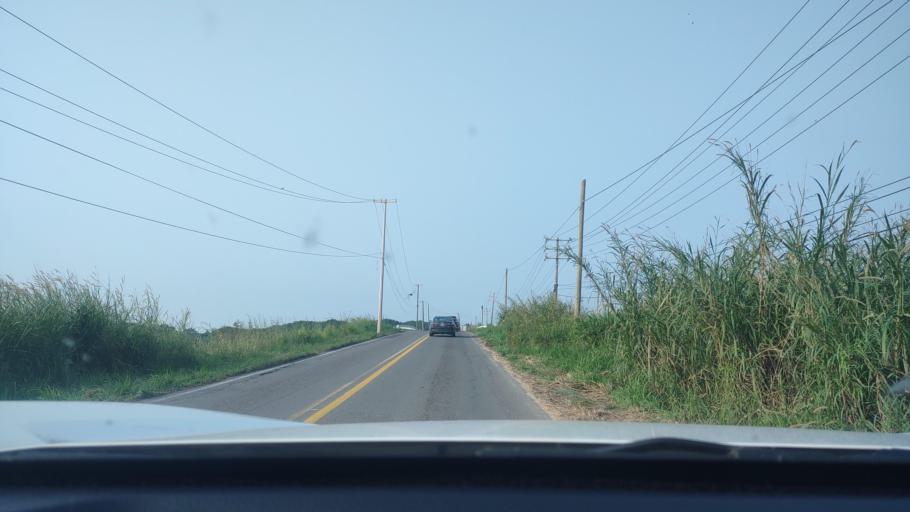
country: MX
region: Veracruz
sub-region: Coatzacoalcos
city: Centro de Readaptacion Social
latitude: 18.1344
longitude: -94.5268
